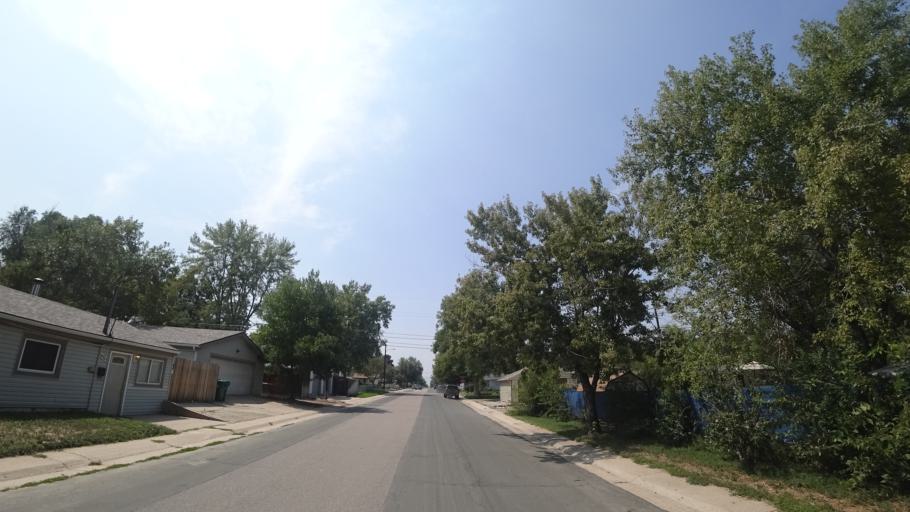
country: US
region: Colorado
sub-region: Arapahoe County
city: Englewood
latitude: 39.6313
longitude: -104.9905
